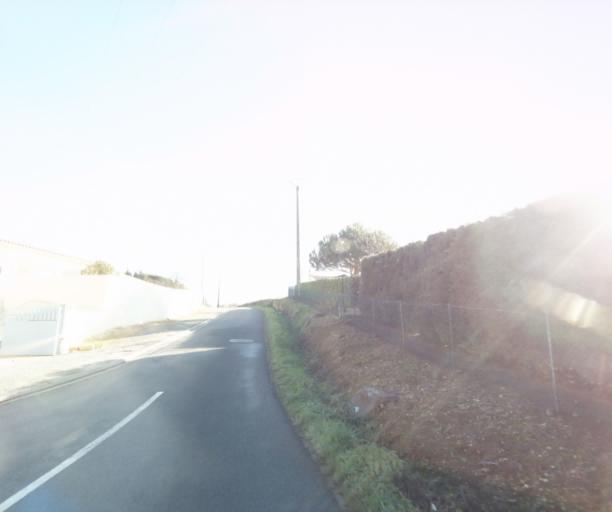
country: FR
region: Poitou-Charentes
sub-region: Departement de la Charente-Maritime
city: Burie
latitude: 45.7731
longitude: -0.4274
